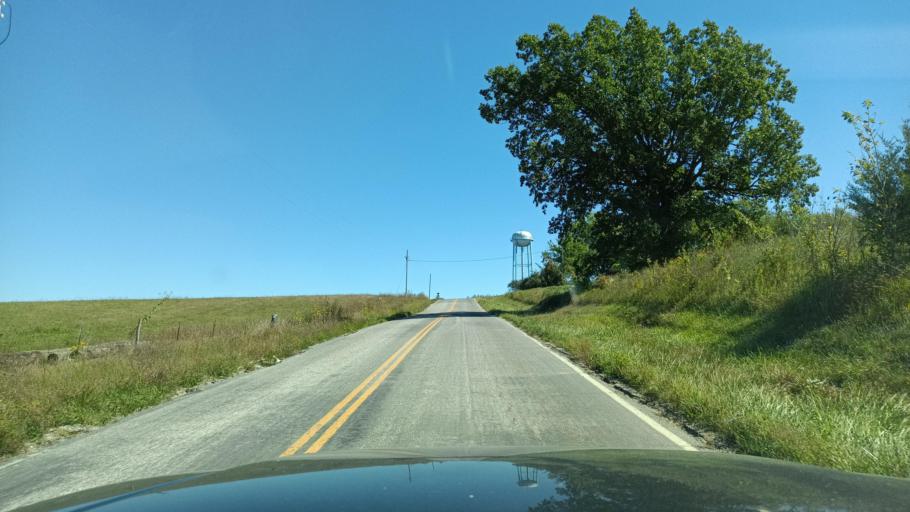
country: US
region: Missouri
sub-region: Macon County
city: La Plata
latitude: 40.0217
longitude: -92.5324
